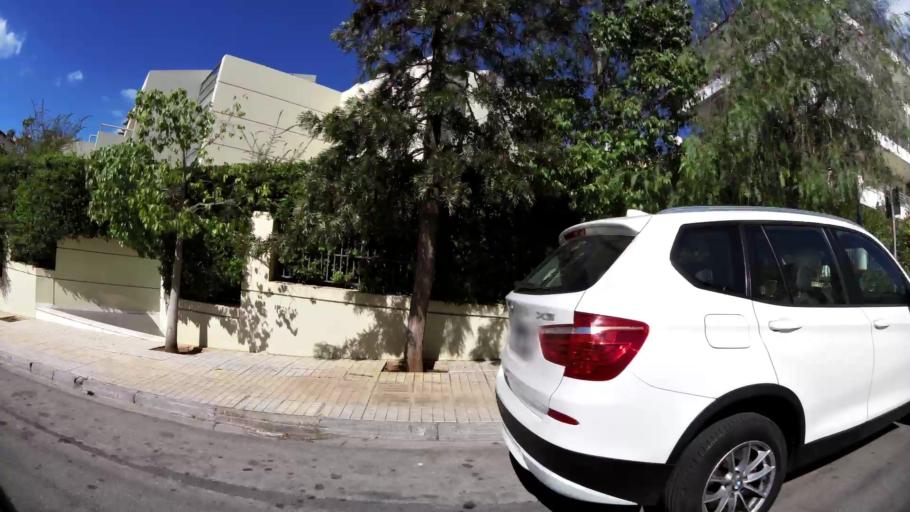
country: GR
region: Attica
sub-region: Nomarchia Anatolikis Attikis
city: Voula
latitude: 37.8527
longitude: 23.7725
